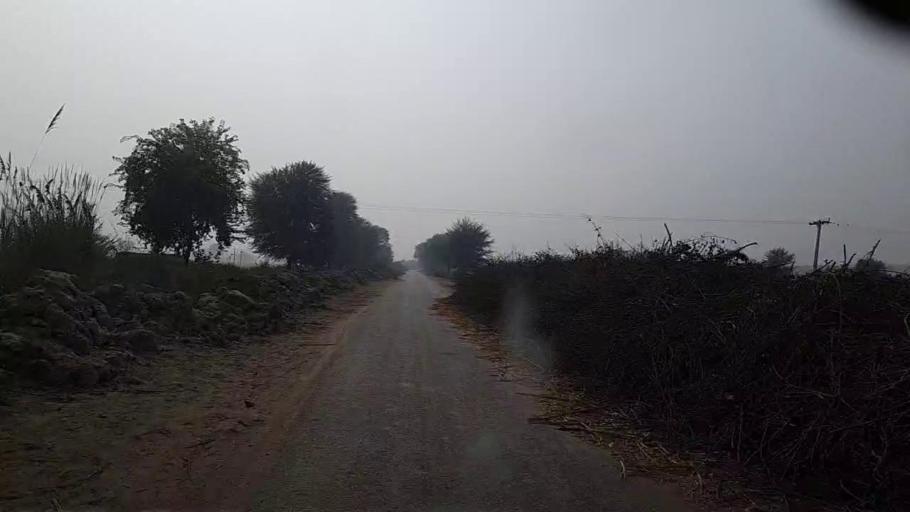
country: PK
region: Sindh
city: Kandiari
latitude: 26.9855
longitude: 68.6032
